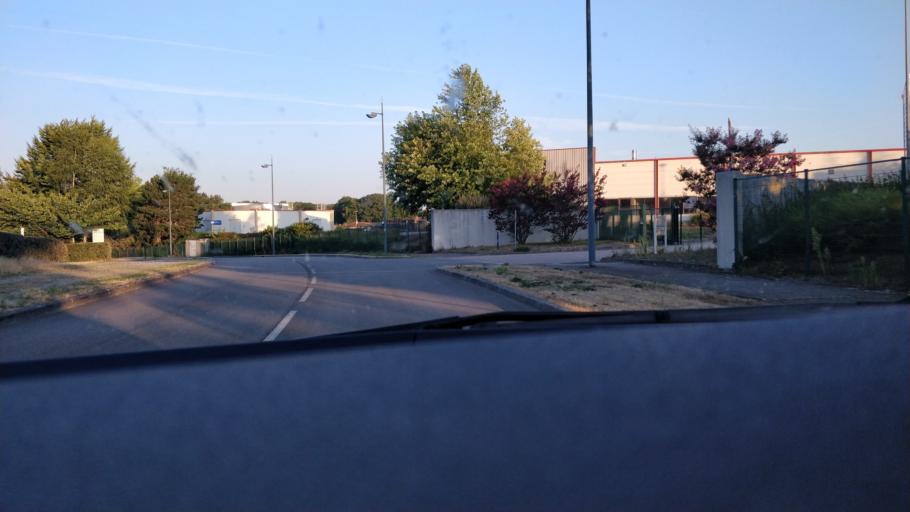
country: FR
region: Limousin
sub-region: Departement de la Haute-Vienne
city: Le Palais-sur-Vienne
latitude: 45.8646
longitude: 1.2954
